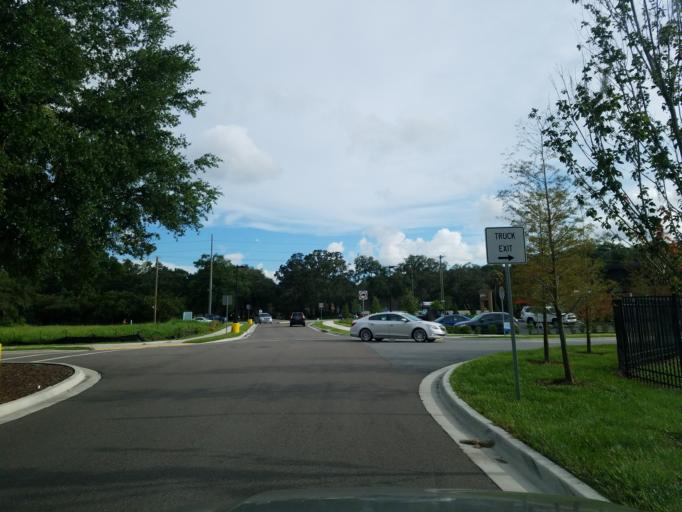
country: US
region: Florida
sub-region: Hillsborough County
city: Bloomingdale
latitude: 27.8947
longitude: -82.2490
